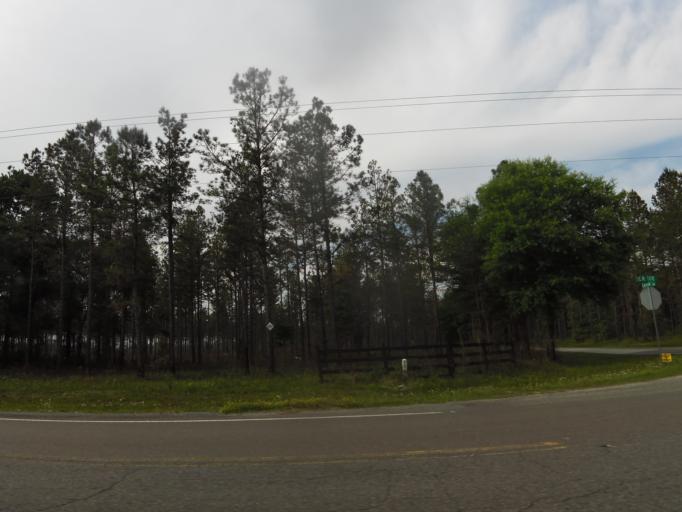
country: US
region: Georgia
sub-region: Camden County
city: Kingsland
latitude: 30.6985
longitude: -81.7780
